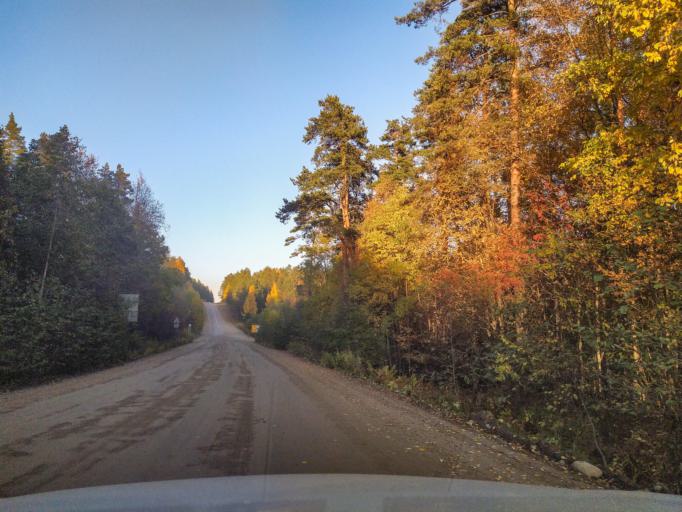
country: RU
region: Leningrad
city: Kuznechnoye
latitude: 61.3304
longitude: 29.9692
